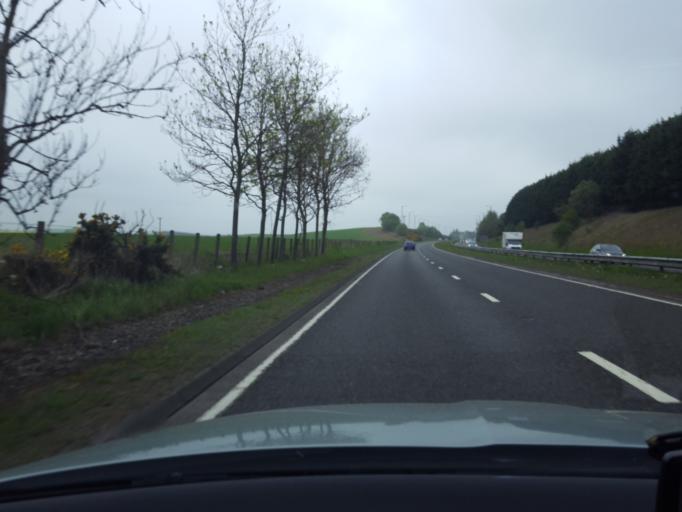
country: GB
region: Scotland
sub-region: Angus
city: Forfar
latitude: 56.6679
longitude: -2.9061
